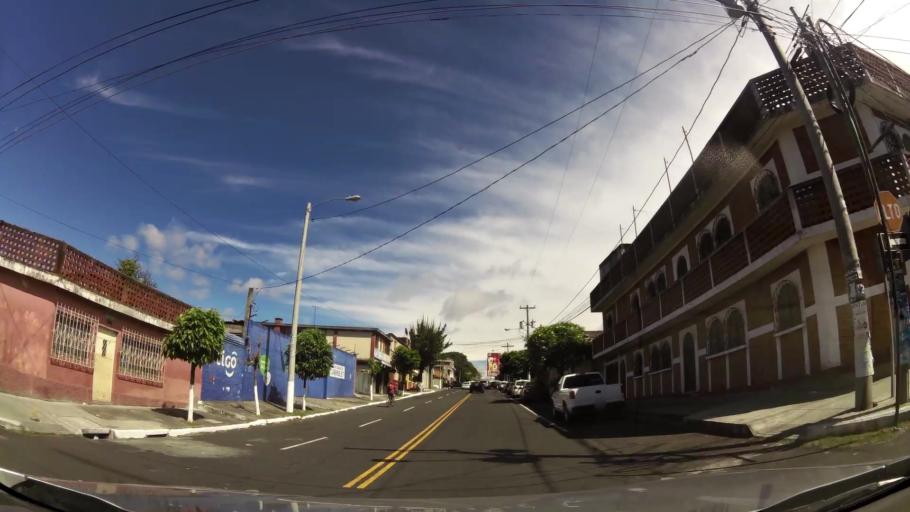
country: GT
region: Guatemala
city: Guatemala City
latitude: 14.6026
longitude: -90.5414
